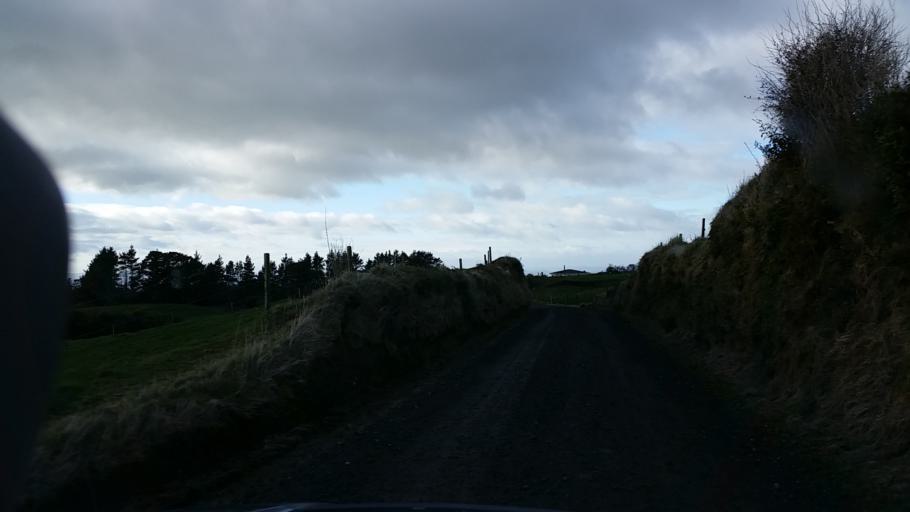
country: NZ
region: Taranaki
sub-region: South Taranaki District
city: Eltham
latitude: -39.3322
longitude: 174.1733
